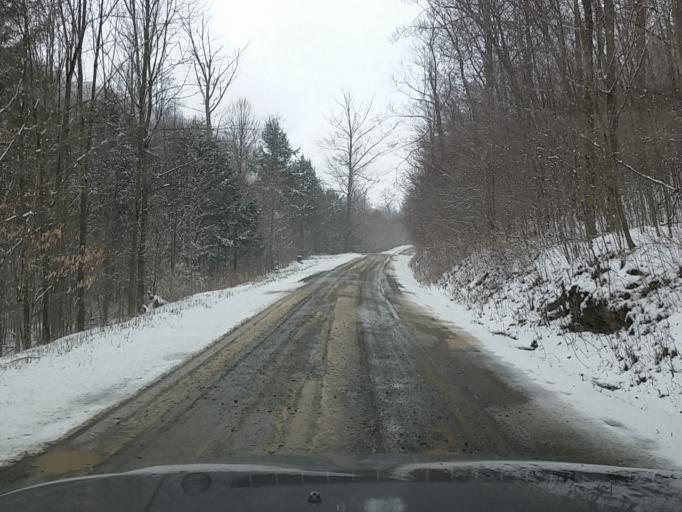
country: US
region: Pennsylvania
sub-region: Sullivan County
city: Laporte
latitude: 41.3285
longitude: -76.4610
